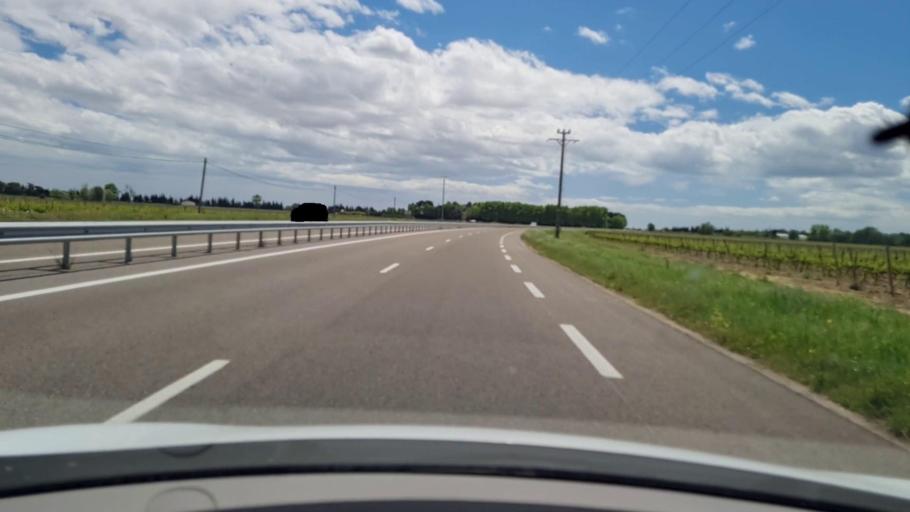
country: FR
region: Languedoc-Roussillon
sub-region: Departement du Gard
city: Aimargues
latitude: 43.6687
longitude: 4.2166
